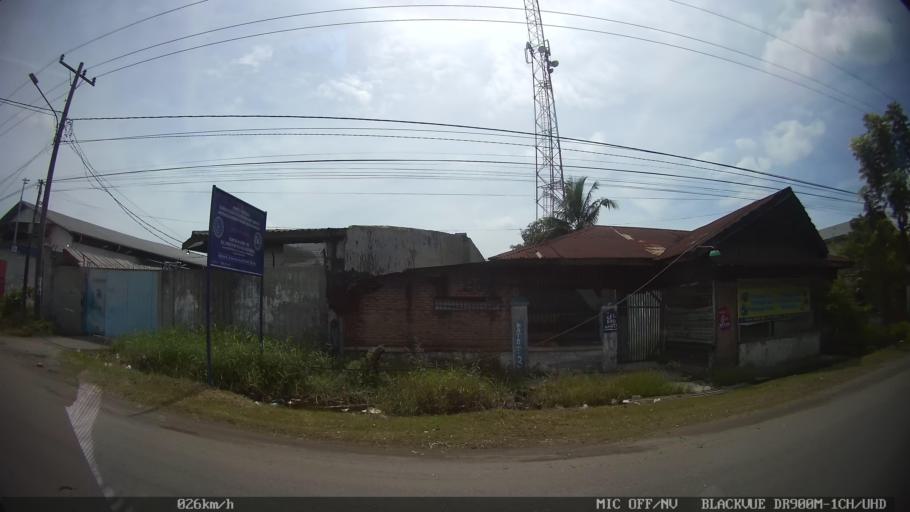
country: ID
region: North Sumatra
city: Medan
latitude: 3.6376
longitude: 98.7166
